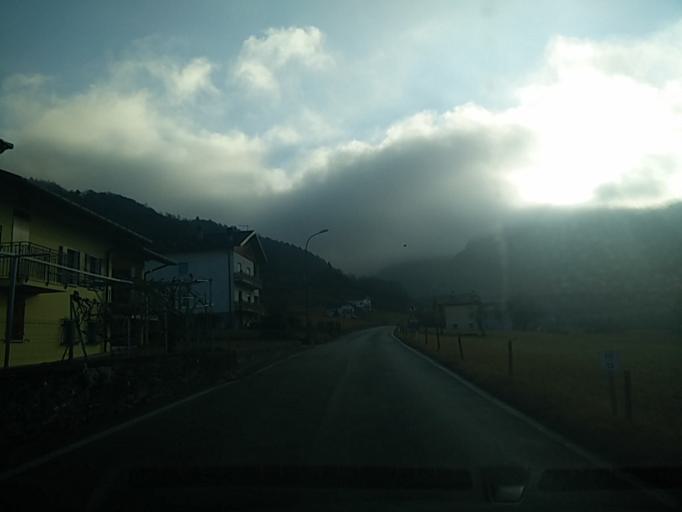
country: IT
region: Veneto
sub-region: Provincia di Belluno
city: Trichiana
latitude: 46.0316
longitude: 12.1636
